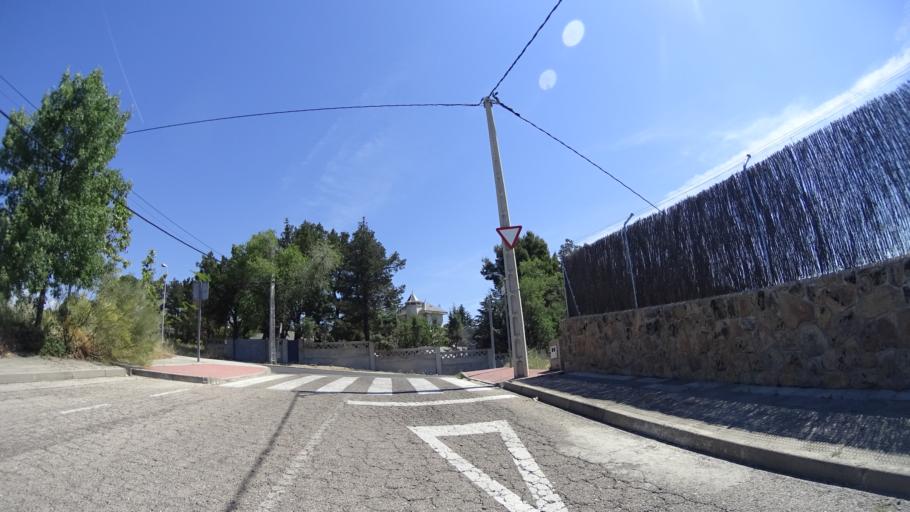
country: ES
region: Madrid
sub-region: Provincia de Madrid
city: Colmenarejo
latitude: 40.5528
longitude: -4.0069
